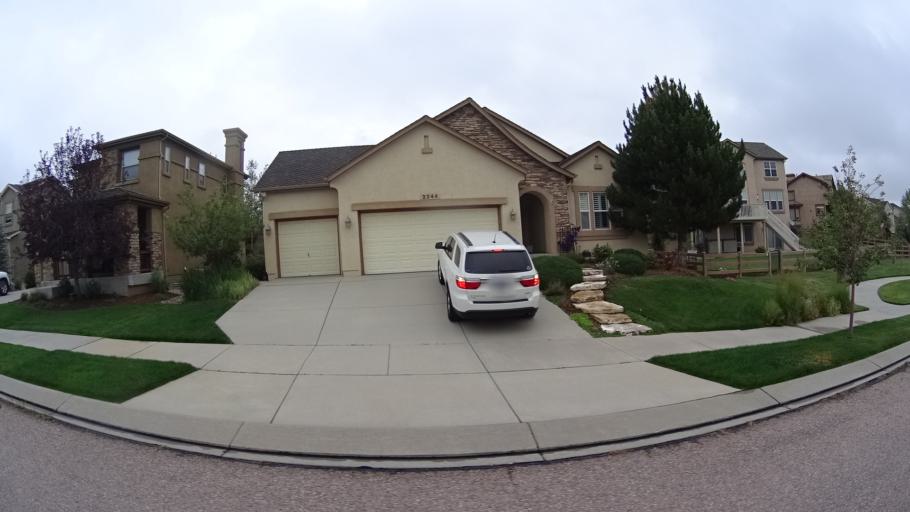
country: US
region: Colorado
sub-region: El Paso County
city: Gleneagle
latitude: 39.0334
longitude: -104.7827
